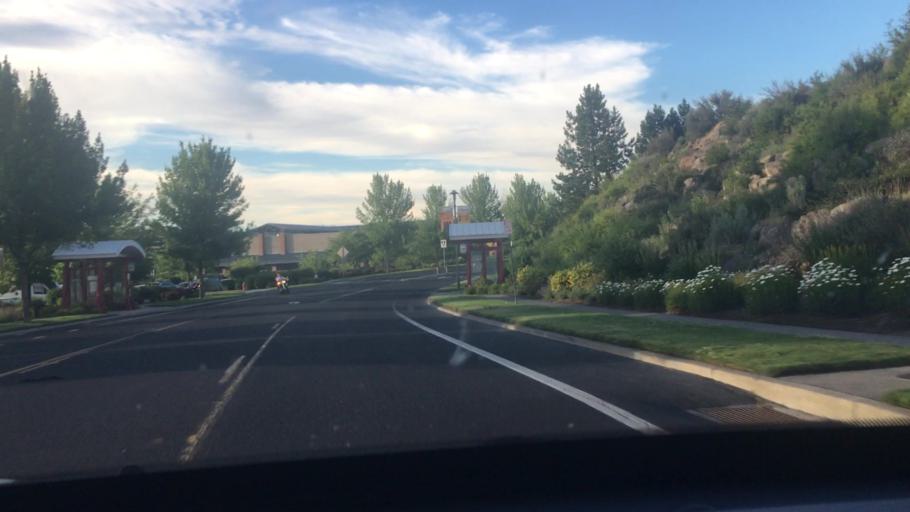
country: US
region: Oregon
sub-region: Deschutes County
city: Bend
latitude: 44.0426
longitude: -121.3141
